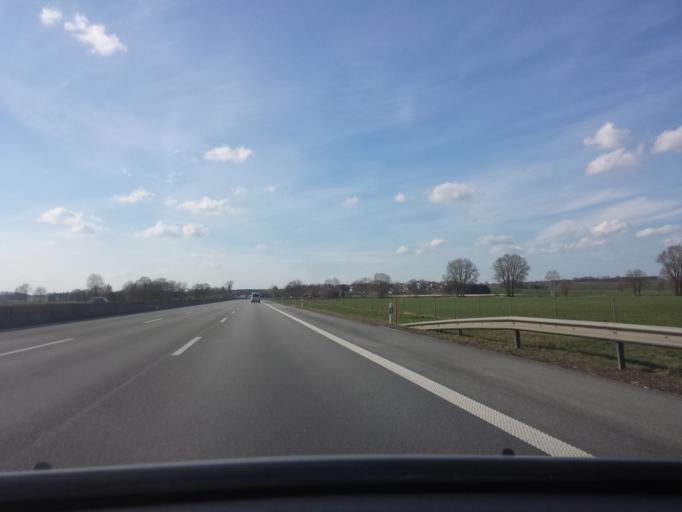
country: DE
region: Bavaria
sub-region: Upper Bavaria
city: Bergkirchen
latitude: 48.2454
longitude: 11.3254
